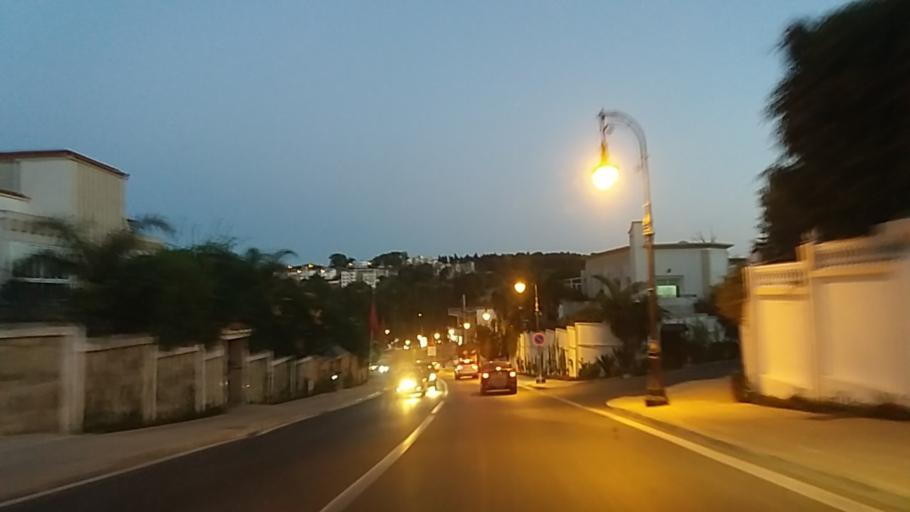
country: MA
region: Tanger-Tetouan
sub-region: Tanger-Assilah
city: Tangier
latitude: 35.7828
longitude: -5.8432
